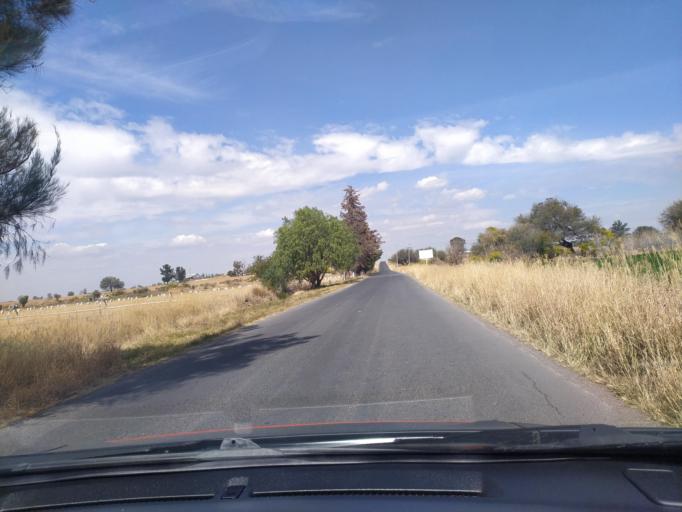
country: MX
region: Guanajuato
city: San Roque
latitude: 20.9543
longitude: -101.8304
